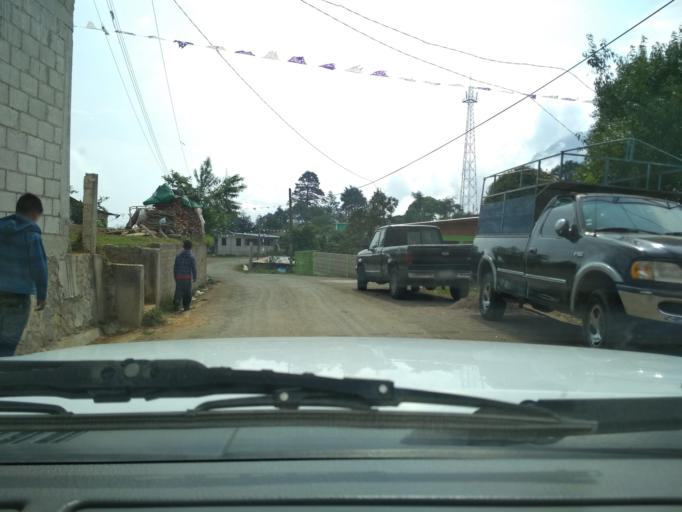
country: MX
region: Veracruz
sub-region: Camerino Z. Mendoza
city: Necoxtla
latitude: 18.7668
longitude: -97.1476
